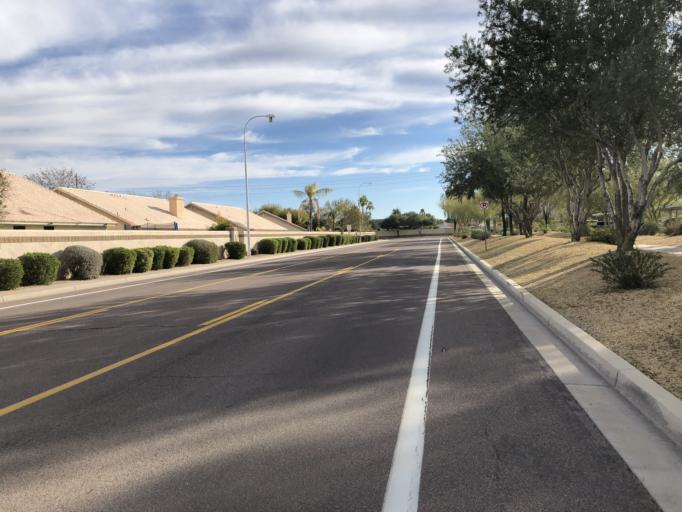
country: US
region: Arizona
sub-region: Maricopa County
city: San Carlos
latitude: 33.3127
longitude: -111.9127
